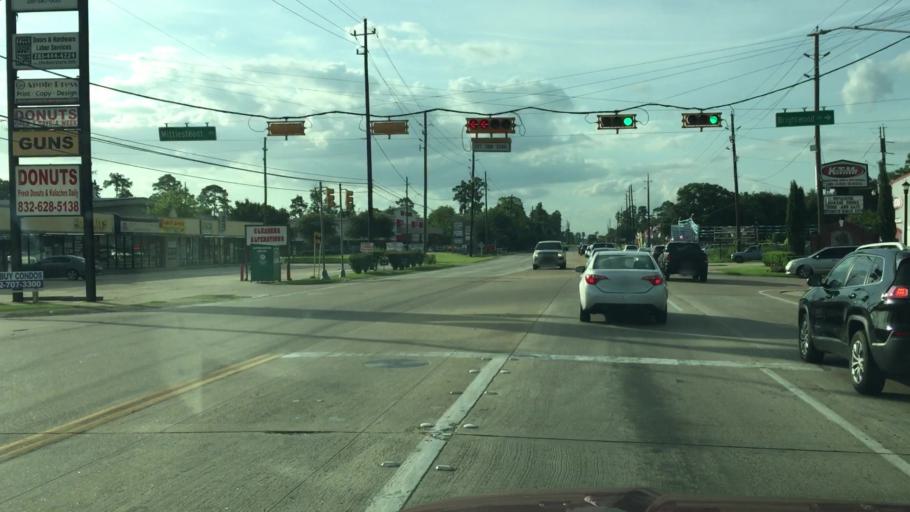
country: US
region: Texas
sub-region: Harris County
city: Hudson
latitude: 29.9988
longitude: -95.5063
